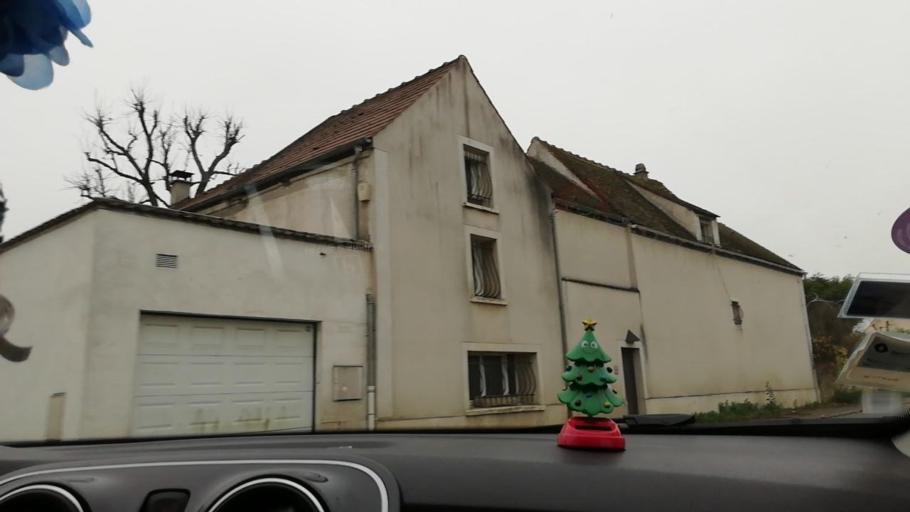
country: FR
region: Ile-de-France
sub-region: Departement de Seine-et-Marne
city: Charny
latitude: 48.9807
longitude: 2.7820
